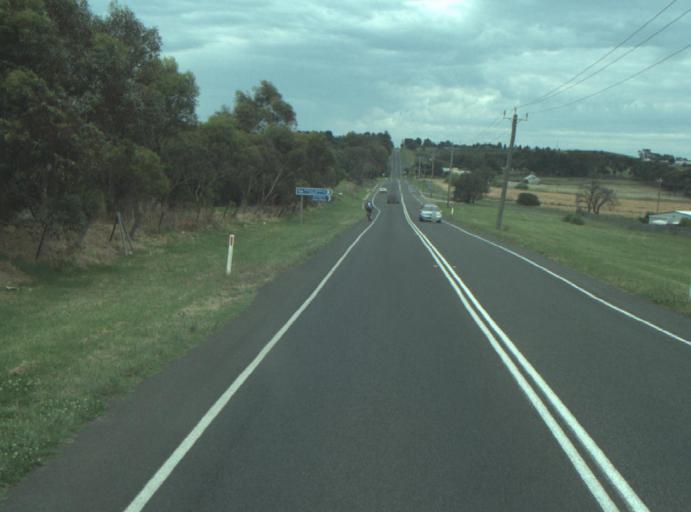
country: AU
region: Victoria
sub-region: Greater Geelong
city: Clifton Springs
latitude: -38.1260
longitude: 144.6292
